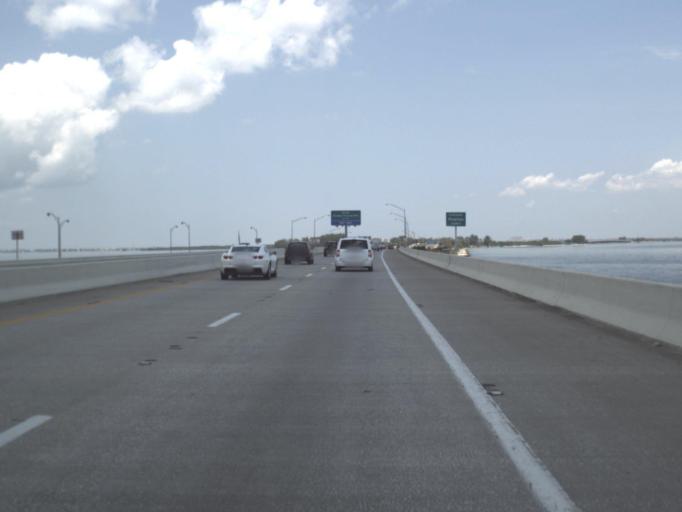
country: US
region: Florida
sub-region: Pinellas County
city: Tierra Verde
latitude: 27.6387
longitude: -82.6687
